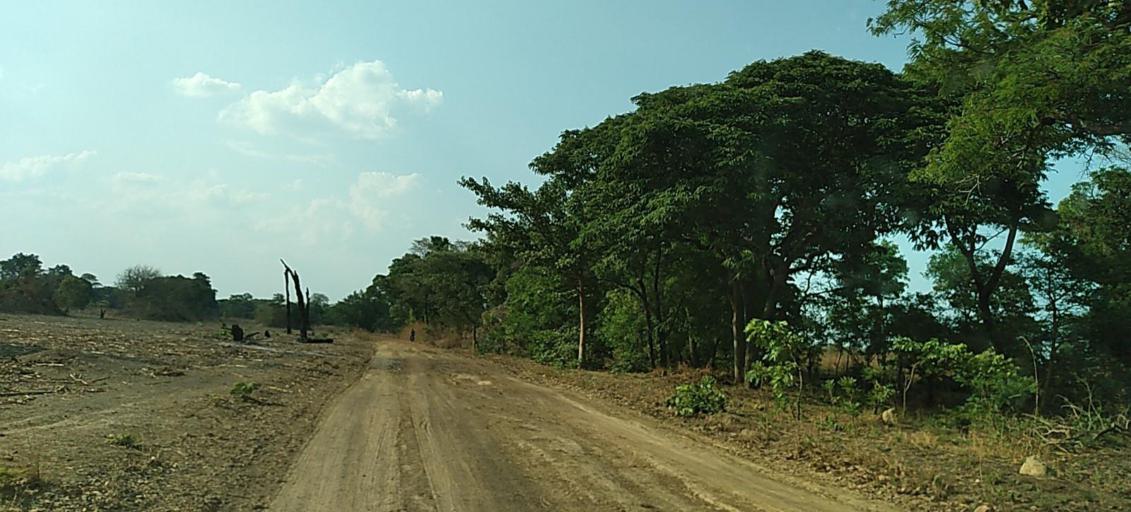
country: ZM
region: Copperbelt
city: Mpongwe
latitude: -13.4554
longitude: 28.0673
